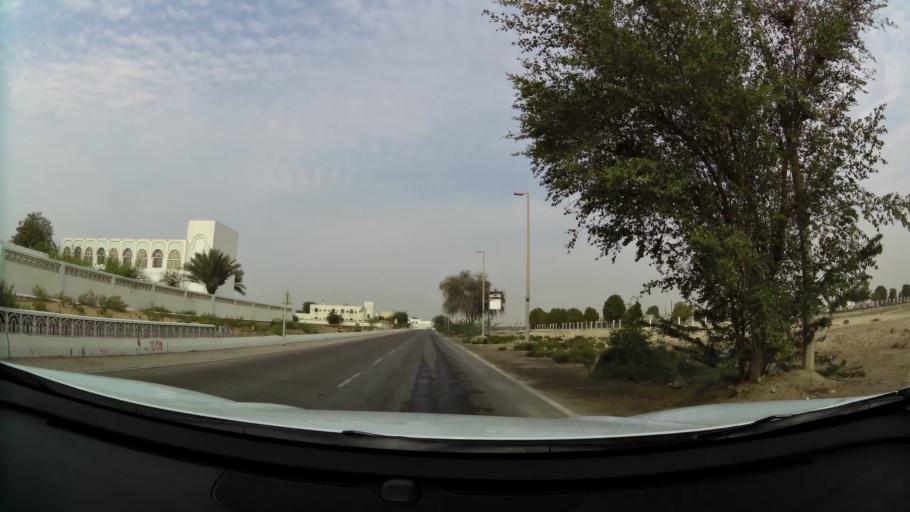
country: AE
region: Abu Dhabi
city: Abu Dhabi
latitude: 24.6784
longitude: 54.7625
